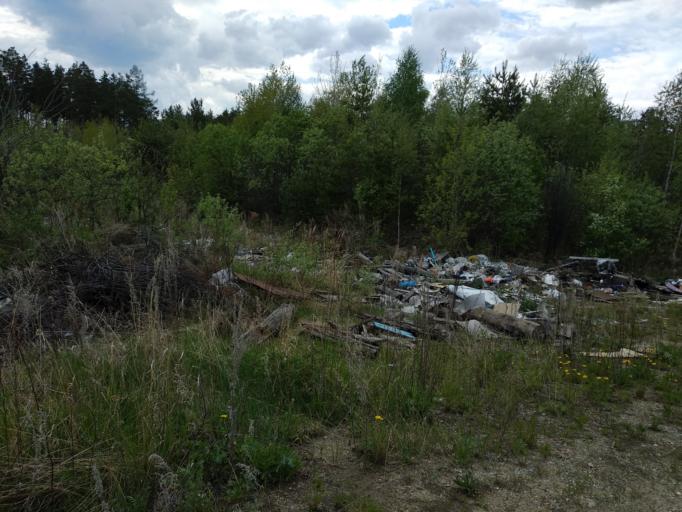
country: RU
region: Sverdlovsk
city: Beryozovsky
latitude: 56.9414
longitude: 60.7233
